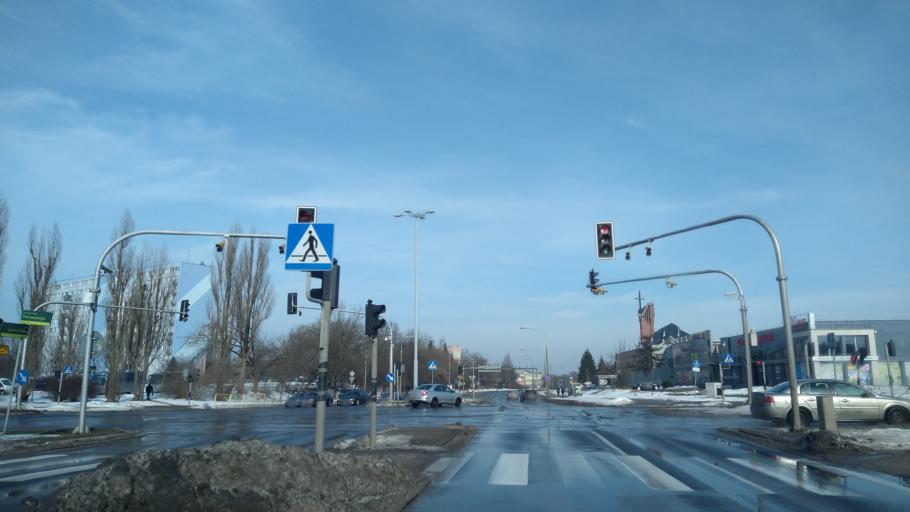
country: PL
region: Warmian-Masurian Voivodeship
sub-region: Powiat olsztynski
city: Olsztyn
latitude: 53.7627
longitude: 20.5009
